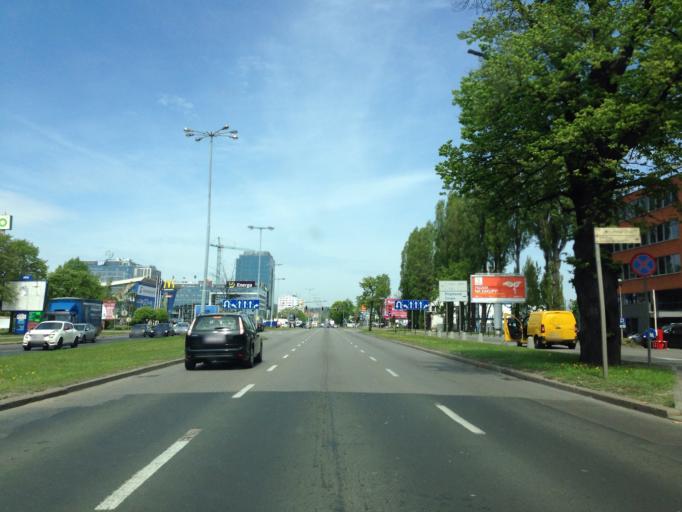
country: PL
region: Pomeranian Voivodeship
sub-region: Sopot
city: Sopot
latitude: 54.3992
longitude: 18.5757
